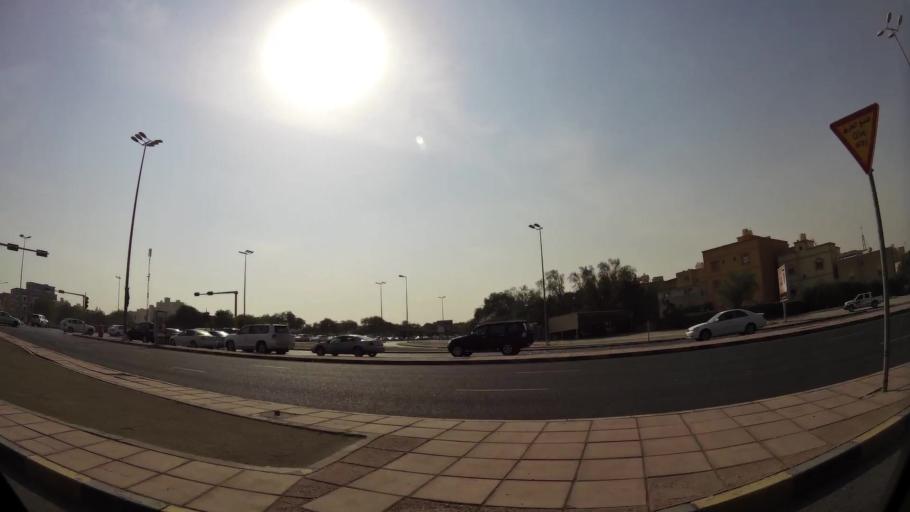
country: KW
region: Al Ahmadi
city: Ar Riqqah
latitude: 29.1573
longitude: 48.0862
